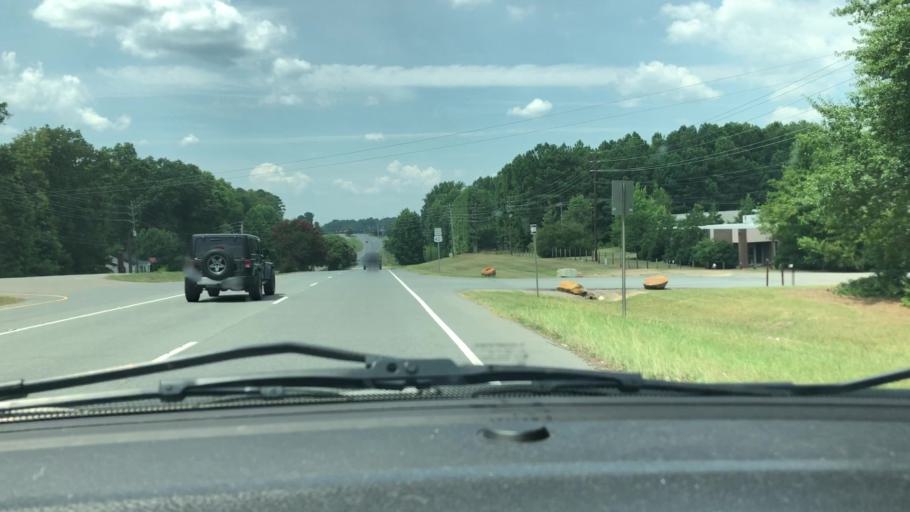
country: US
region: North Carolina
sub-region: Lee County
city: Sanford
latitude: 35.5072
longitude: -79.2091
